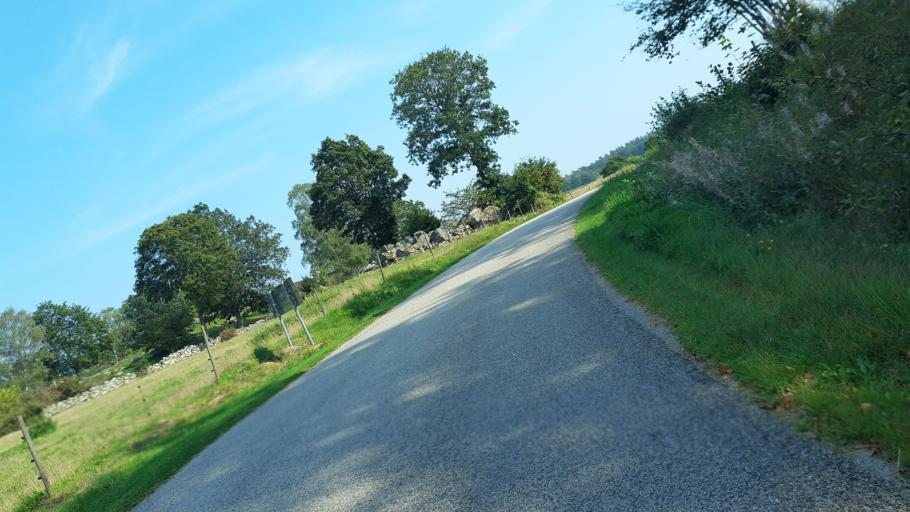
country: SE
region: Blekinge
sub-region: Ronneby Kommun
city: Brakne-Hoby
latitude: 56.1974
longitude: 15.1028
